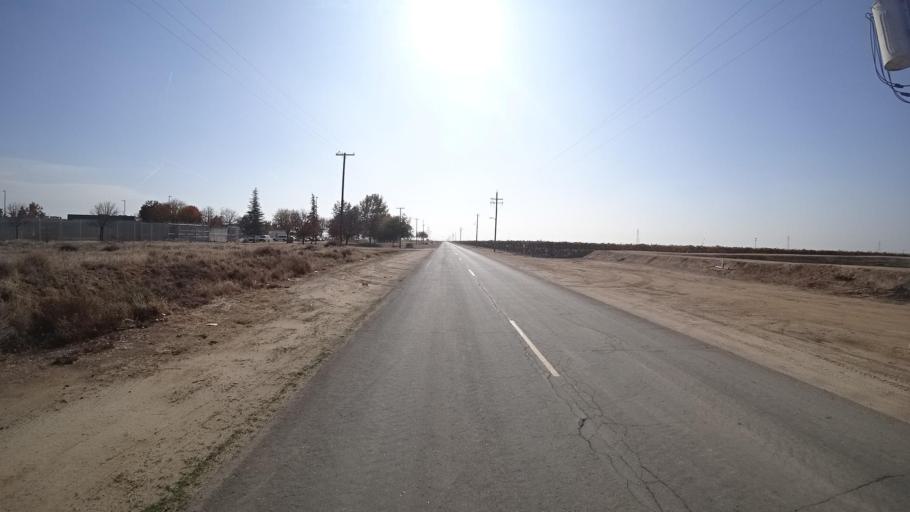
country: US
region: California
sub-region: Kern County
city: Greenacres
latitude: 35.5066
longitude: -119.1167
